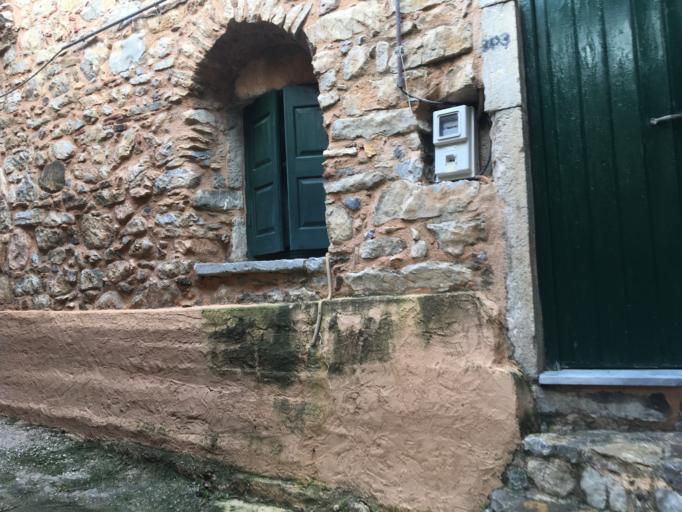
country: GR
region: North Aegean
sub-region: Chios
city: Thymiana
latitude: 38.2463
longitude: 25.9422
